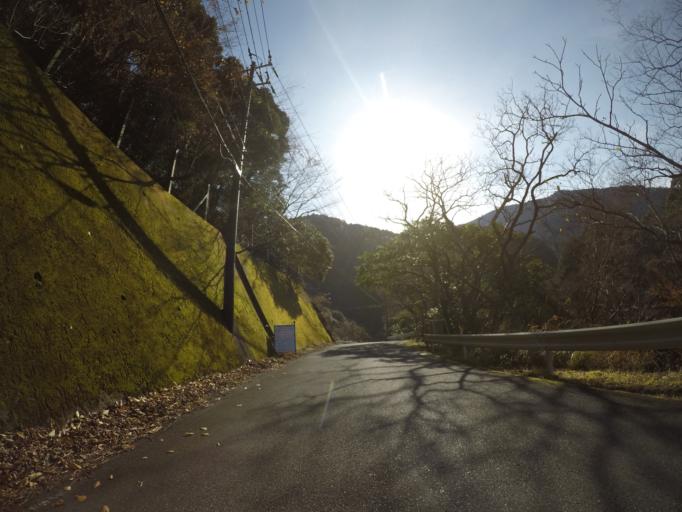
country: JP
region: Shizuoka
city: Heda
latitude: 34.8079
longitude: 138.8235
